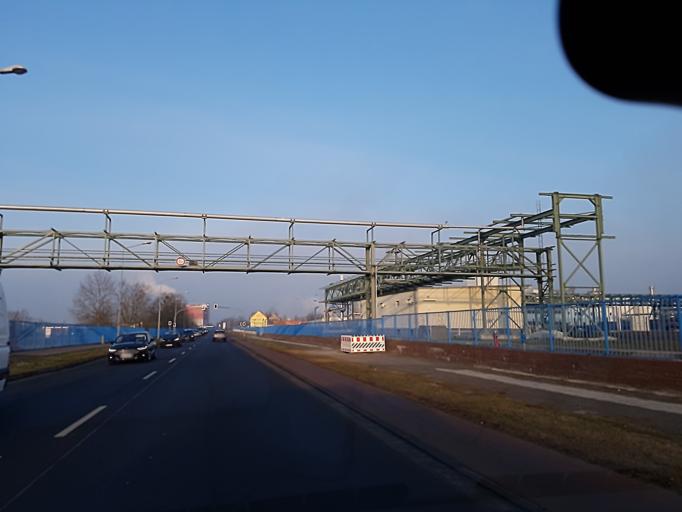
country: DE
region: Saxony-Anhalt
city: Wittenburg
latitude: 51.8692
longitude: 12.5807
